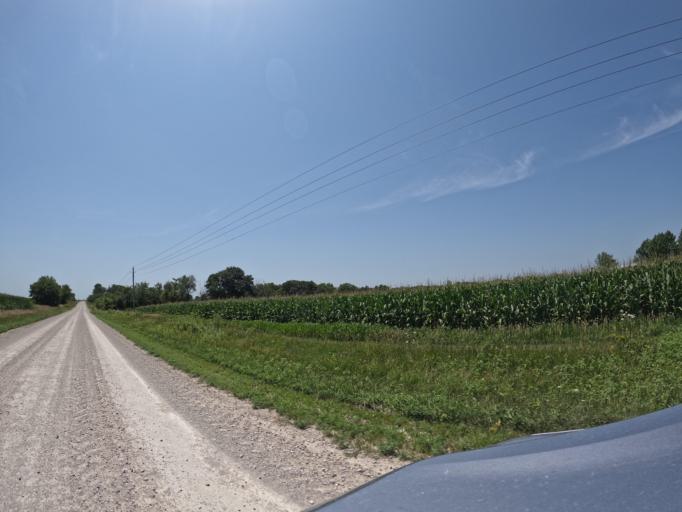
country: US
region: Iowa
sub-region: Henry County
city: Mount Pleasant
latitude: 40.9167
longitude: -91.6461
